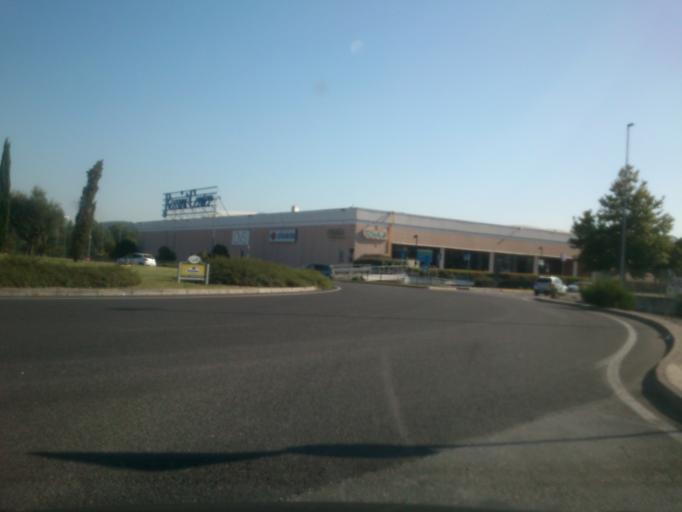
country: IT
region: The Marches
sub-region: Provincia di Pesaro e Urbino
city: Pesaro
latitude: 43.9069
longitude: 12.8695
